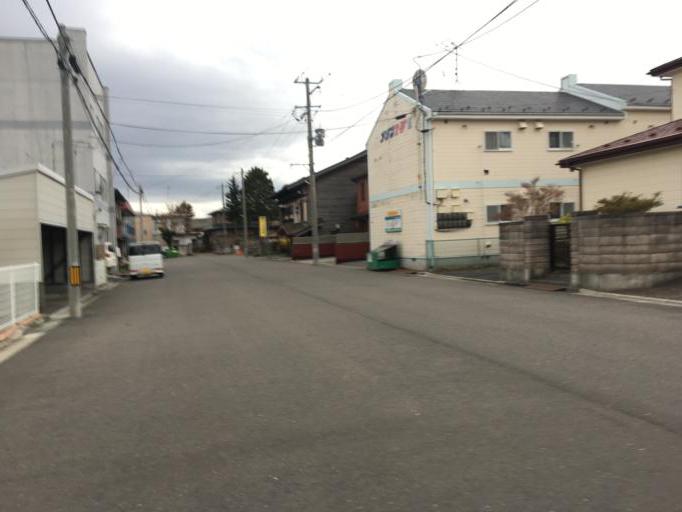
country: JP
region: Aomori
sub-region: Hachinohe Shi
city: Uchimaru
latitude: 40.5201
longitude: 141.5184
